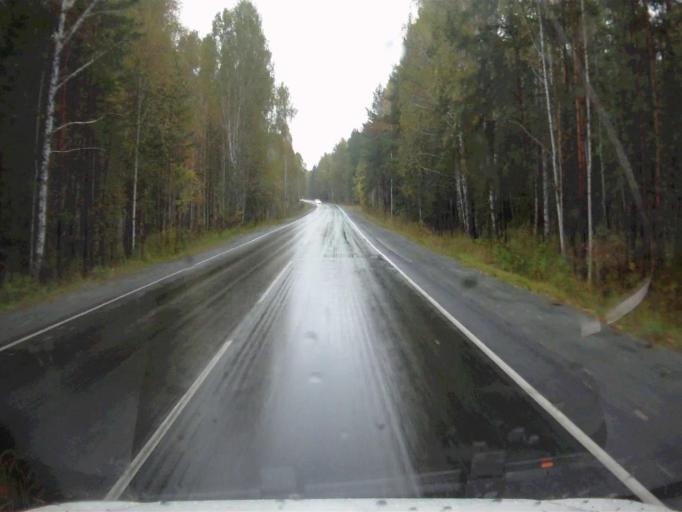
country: RU
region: Chelyabinsk
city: Tayginka
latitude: 55.5920
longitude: 60.6262
